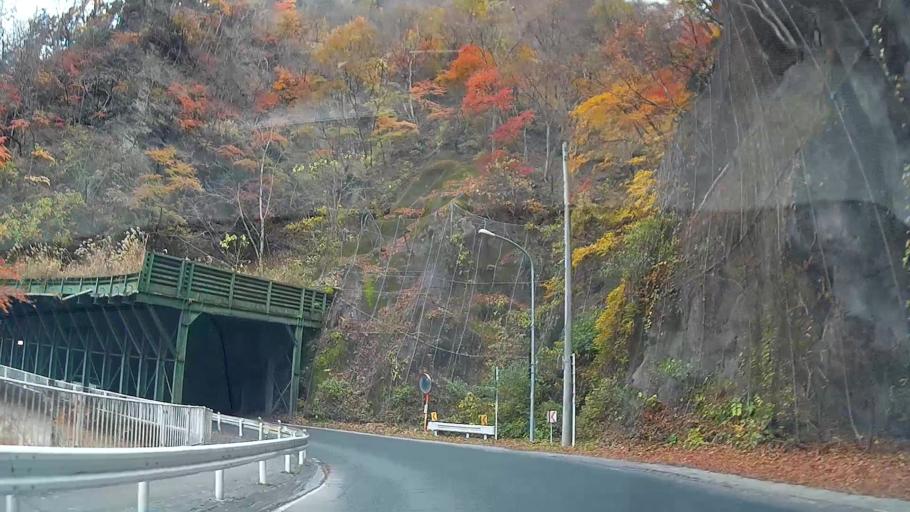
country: JP
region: Saitama
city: Chichibu
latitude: 35.9439
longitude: 138.9668
